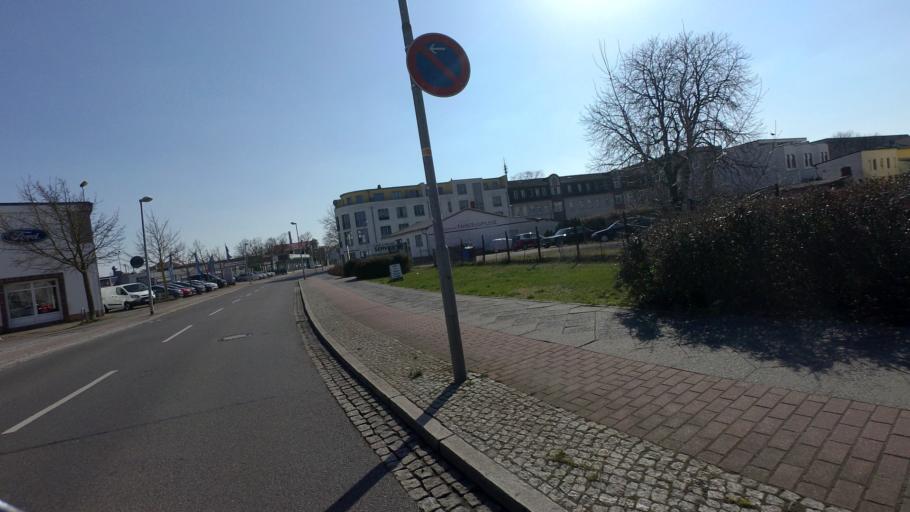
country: DE
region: Brandenburg
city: Hennigsdorf
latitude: 52.6427
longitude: 13.2103
